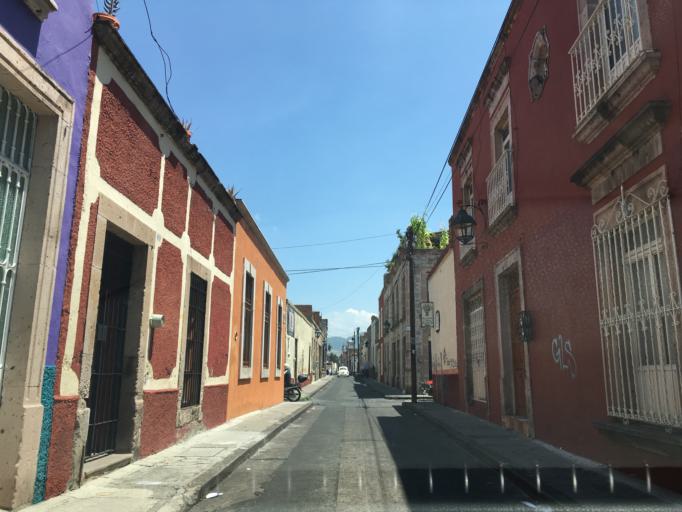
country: MX
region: Michoacan
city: Morelia
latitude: 19.7070
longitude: -101.1876
